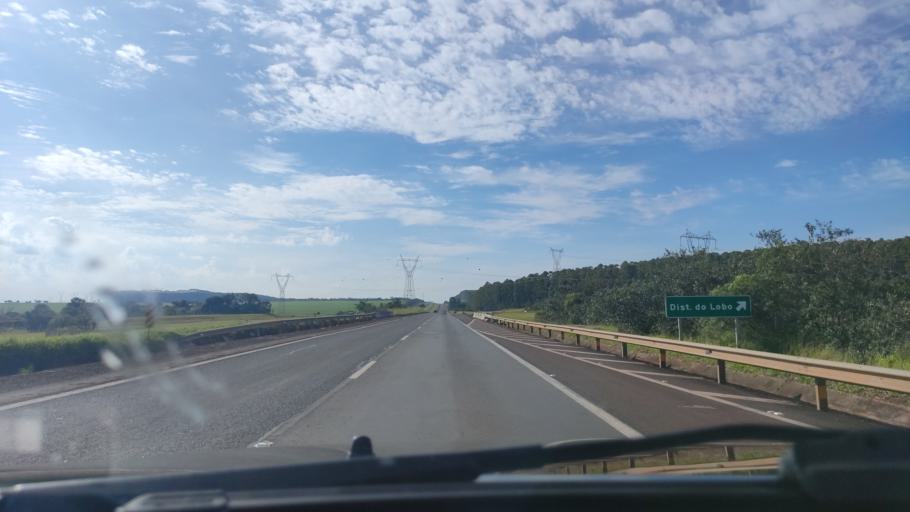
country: BR
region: Sao Paulo
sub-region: Itatinga
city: Itatinga
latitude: -23.0097
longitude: -48.7078
